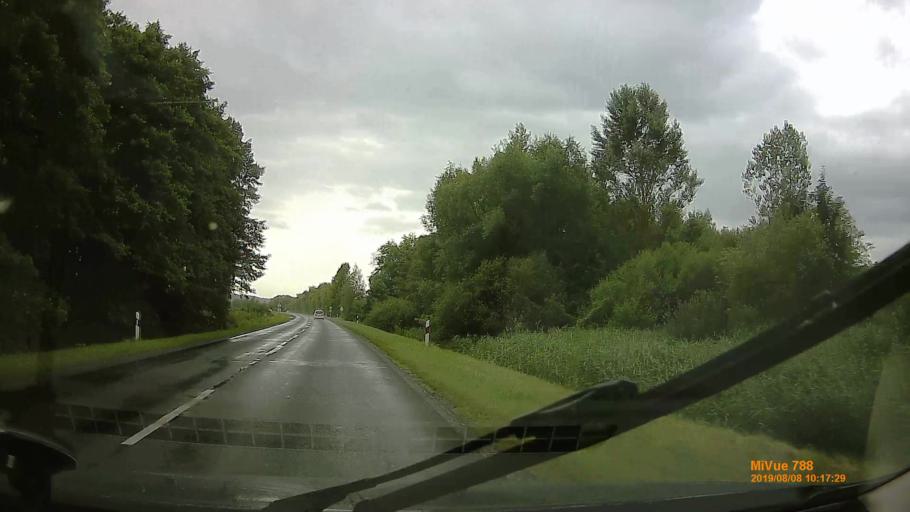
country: HU
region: Zala
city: Zalaegerszeg
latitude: 46.7883
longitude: 16.8546
